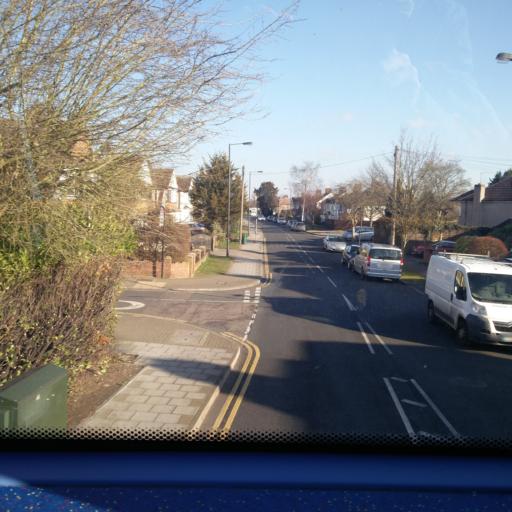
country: GB
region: England
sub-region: Greater London
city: Pinner
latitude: 51.5785
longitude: -0.3823
